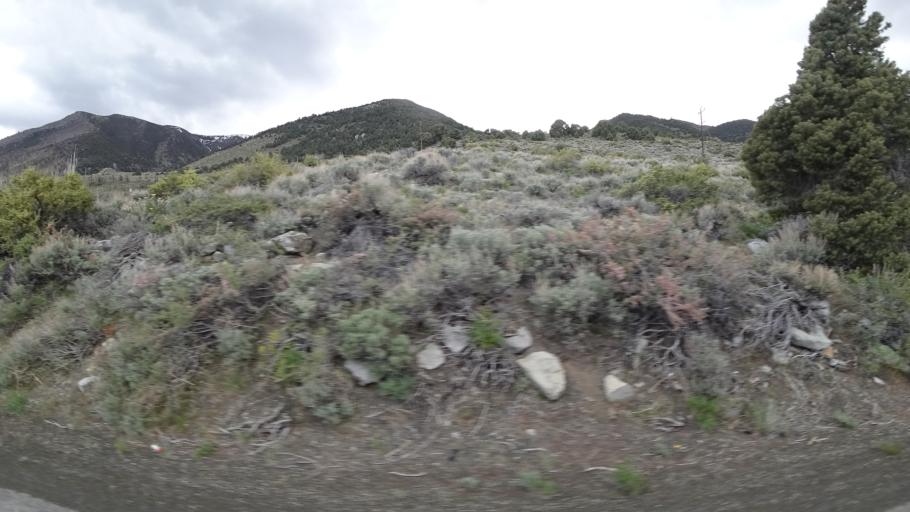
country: US
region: California
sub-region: Mono County
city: Bridgeport
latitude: 37.9973
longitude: -119.1456
